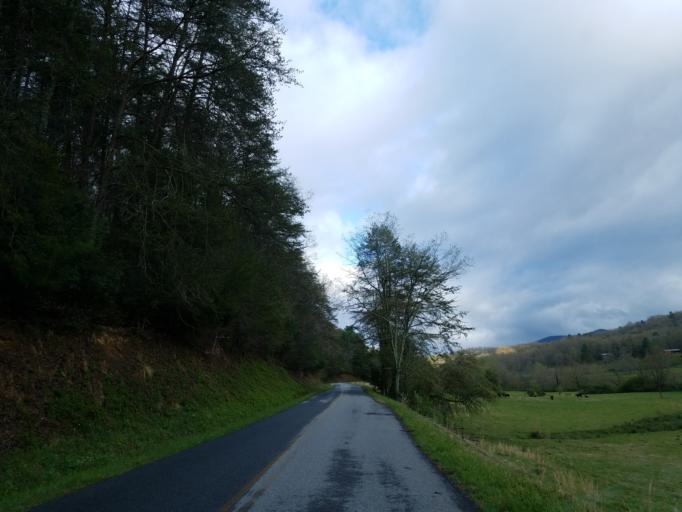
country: US
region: Georgia
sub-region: Fannin County
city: Blue Ridge
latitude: 34.7632
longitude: -84.2225
